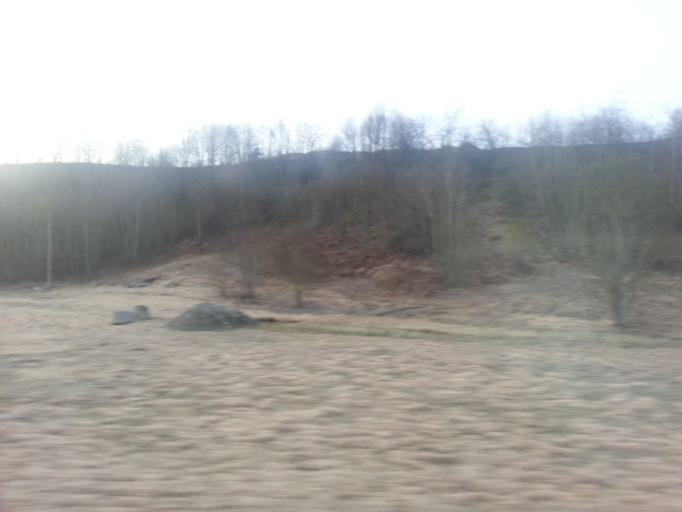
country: NO
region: Sor-Trondelag
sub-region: Melhus
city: Lundamo
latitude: 63.1724
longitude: 10.3041
